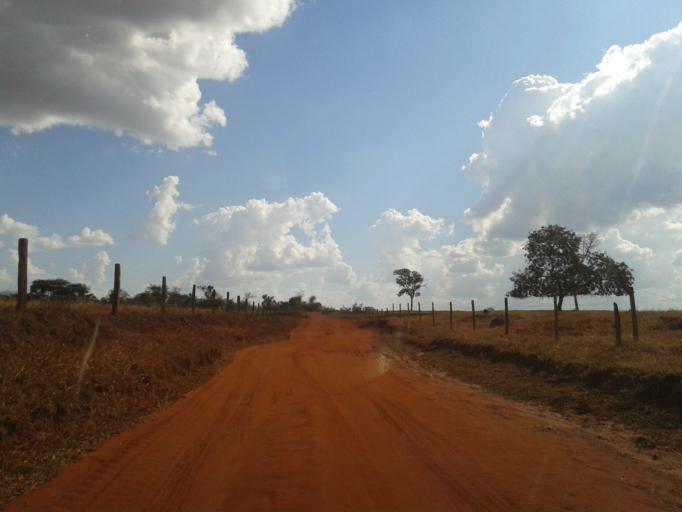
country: BR
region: Minas Gerais
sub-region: Santa Vitoria
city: Santa Vitoria
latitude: -19.2743
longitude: -49.9968
